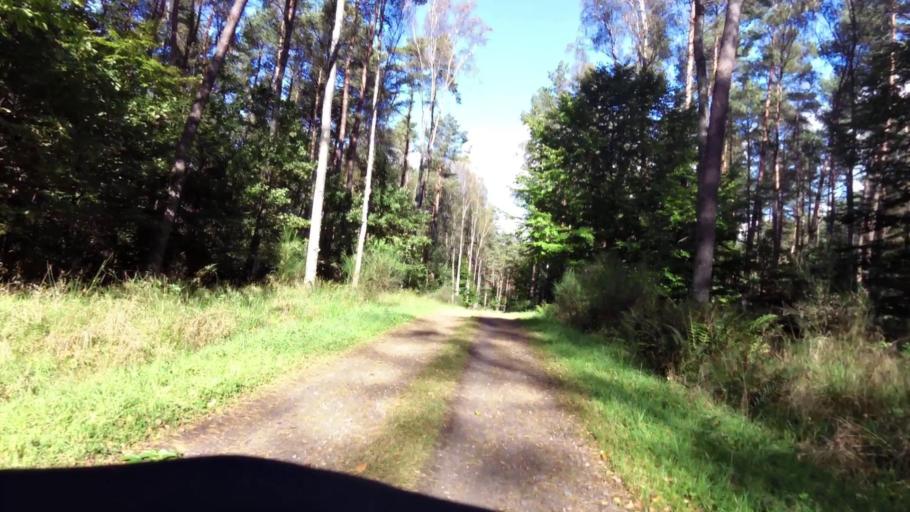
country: PL
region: West Pomeranian Voivodeship
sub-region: Powiat bialogardzki
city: Tychowo
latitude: 54.0200
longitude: 16.1453
